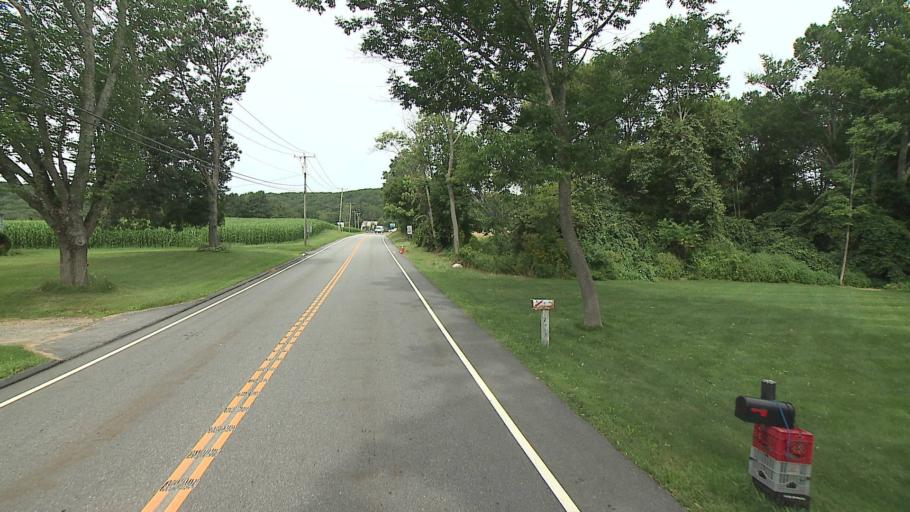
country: US
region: Connecticut
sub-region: Litchfield County
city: New Preston
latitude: 41.7249
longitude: -73.3383
